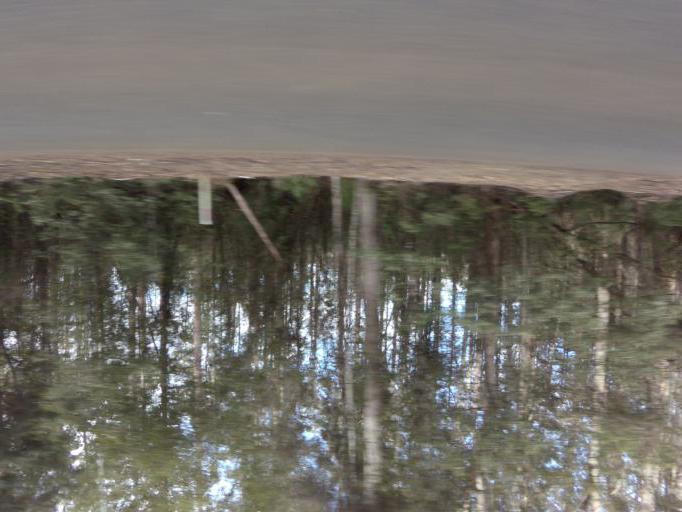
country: AU
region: Tasmania
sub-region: Huon Valley
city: Geeveston
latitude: -43.3844
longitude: 146.9616
